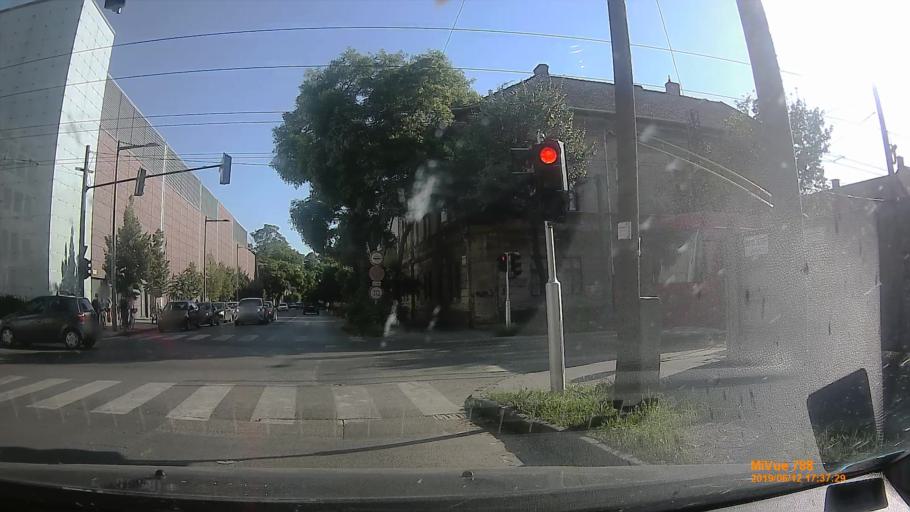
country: HU
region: Csongrad
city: Szeged
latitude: 46.2558
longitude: 20.1369
